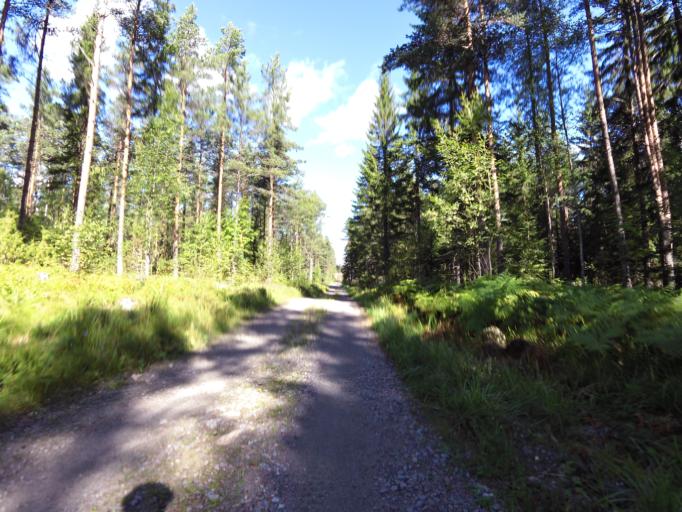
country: SE
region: Gaevleborg
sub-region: Gavle Kommun
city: Valbo
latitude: 60.7256
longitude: 17.0001
